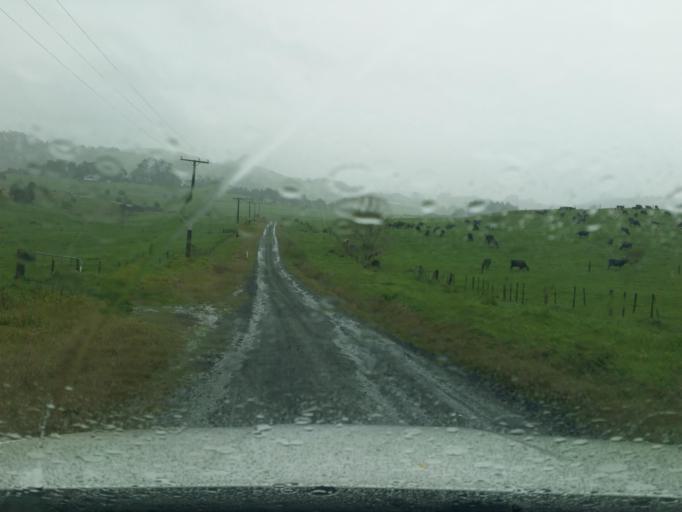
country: NZ
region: Northland
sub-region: Kaipara District
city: Dargaville
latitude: -35.8814
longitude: 173.9965
